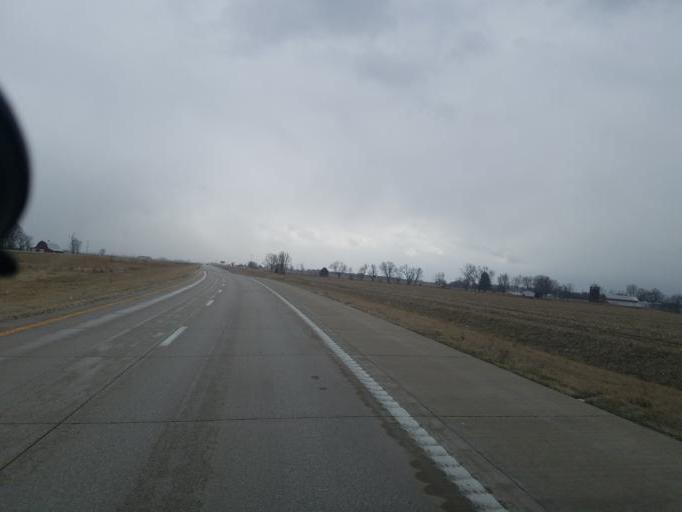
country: US
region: Missouri
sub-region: Randolph County
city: Huntsville
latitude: 39.5727
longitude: -92.4654
